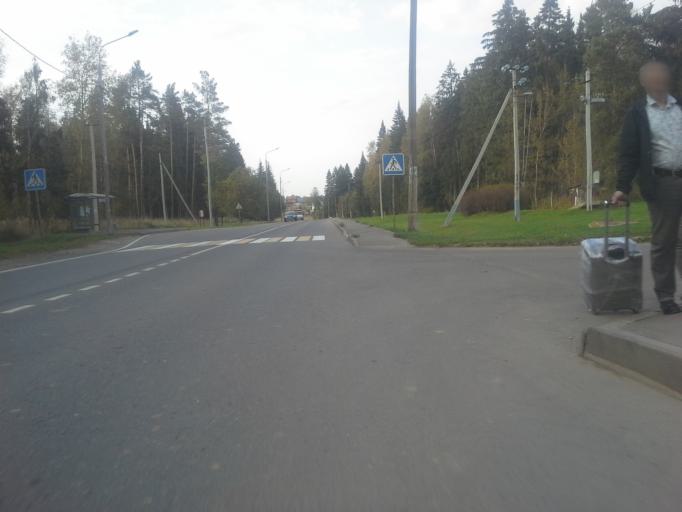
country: RU
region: Moskovskaya
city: Selyatino
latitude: 55.4444
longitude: 36.9500
